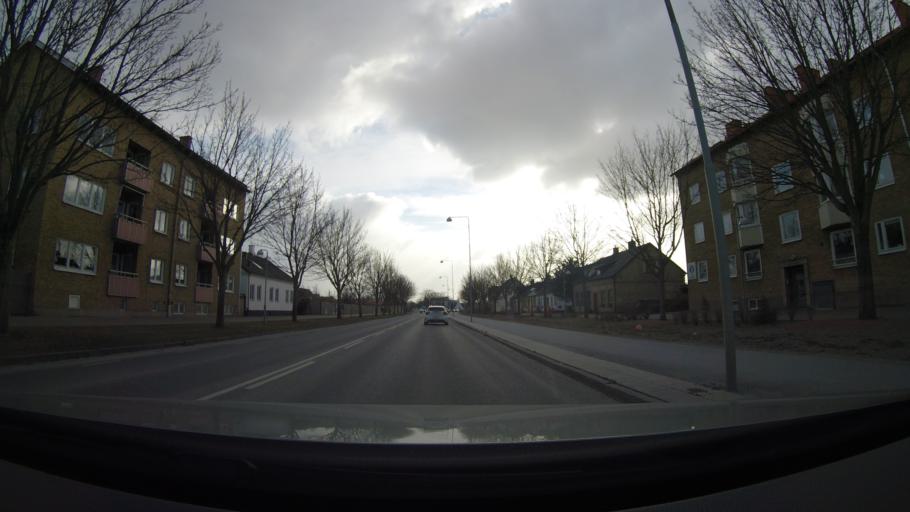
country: SE
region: Skane
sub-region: Malmo
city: Bunkeflostrand
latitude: 55.5809
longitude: 12.9294
